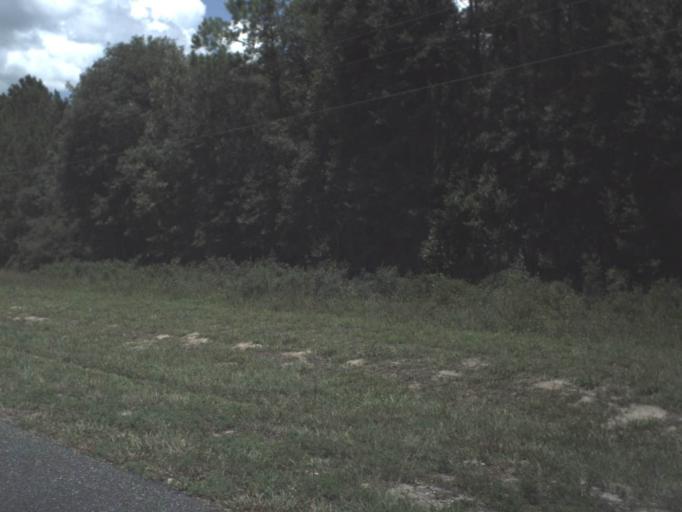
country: US
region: Florida
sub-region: Taylor County
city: Perry
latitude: 30.0060
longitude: -83.5136
